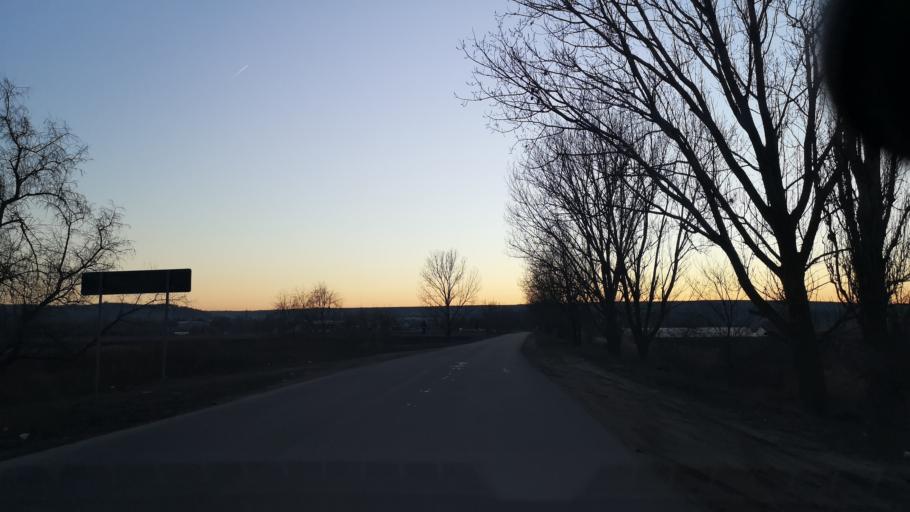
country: MD
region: Anenii Noi
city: Anenii Noi
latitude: 46.8900
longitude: 29.2407
